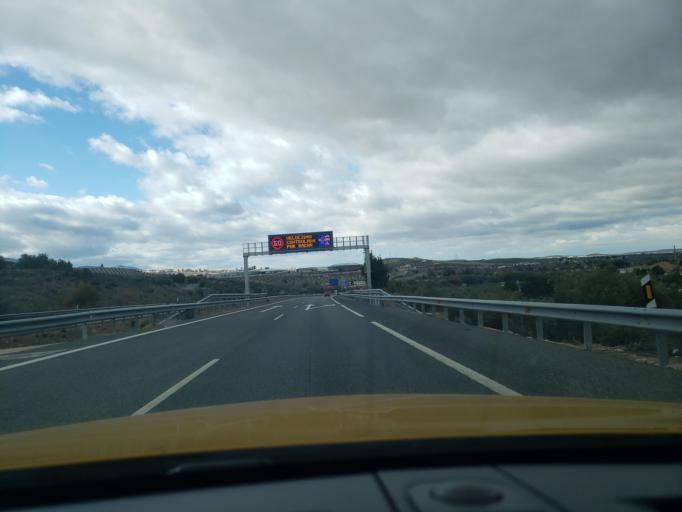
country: ES
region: Andalusia
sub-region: Provincia de Jaen
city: Jaen
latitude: 37.7722
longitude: -3.7384
